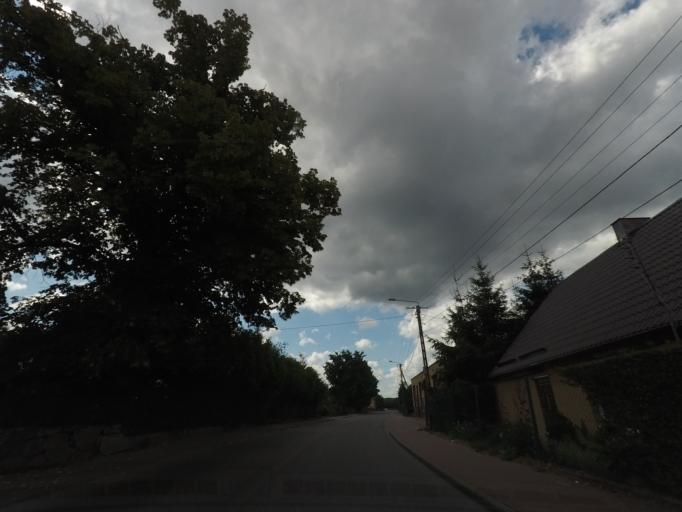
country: PL
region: Pomeranian Voivodeship
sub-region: Powiat wejherowski
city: Leczyce
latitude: 54.5899
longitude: 17.8622
